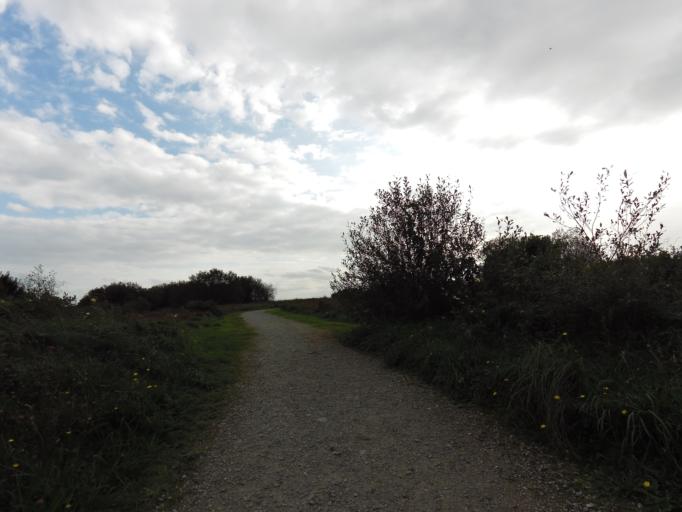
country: IE
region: Leinster
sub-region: Uibh Fhaili
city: Ferbane
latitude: 53.2211
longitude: -7.7280
